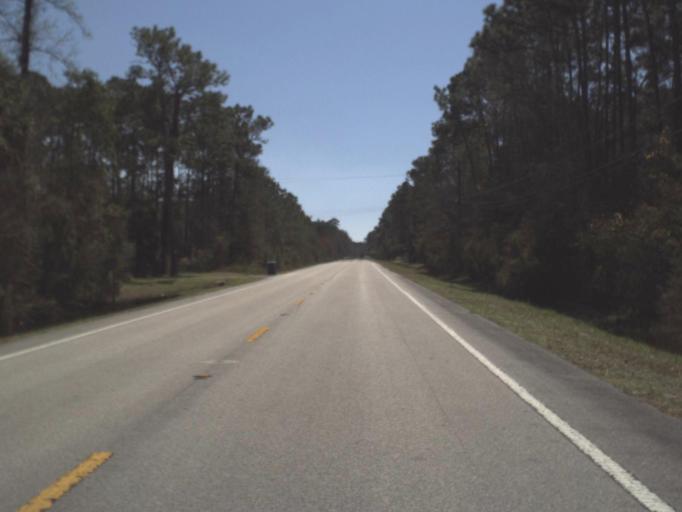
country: US
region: Florida
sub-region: Leon County
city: Woodville
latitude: 30.1825
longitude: -84.2129
